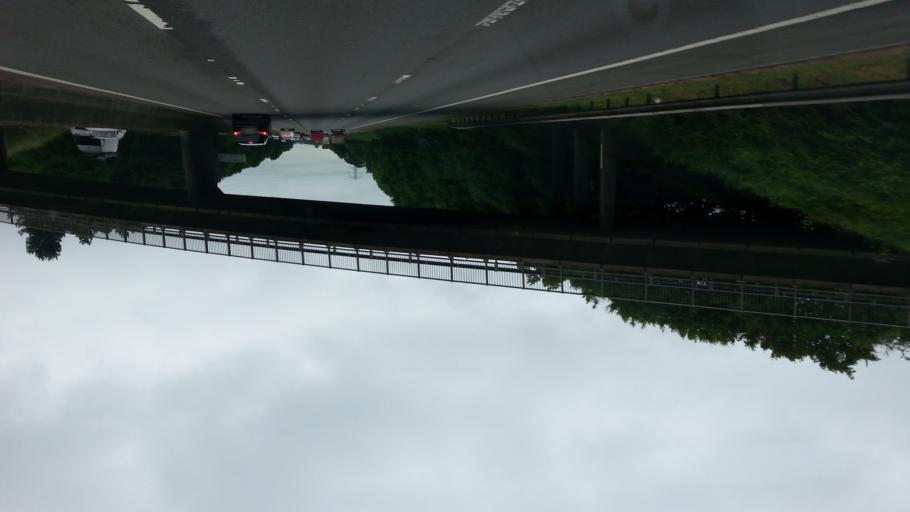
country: GB
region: England
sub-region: Leicestershire
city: Lutterworth
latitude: 52.4778
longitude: -1.1921
